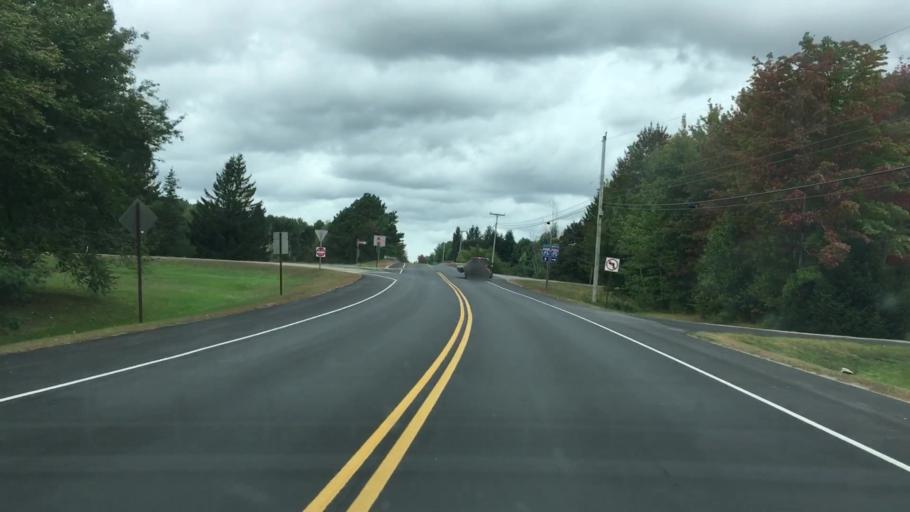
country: US
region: Maine
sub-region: Penobscot County
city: Milford
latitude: 44.9582
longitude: -68.7050
